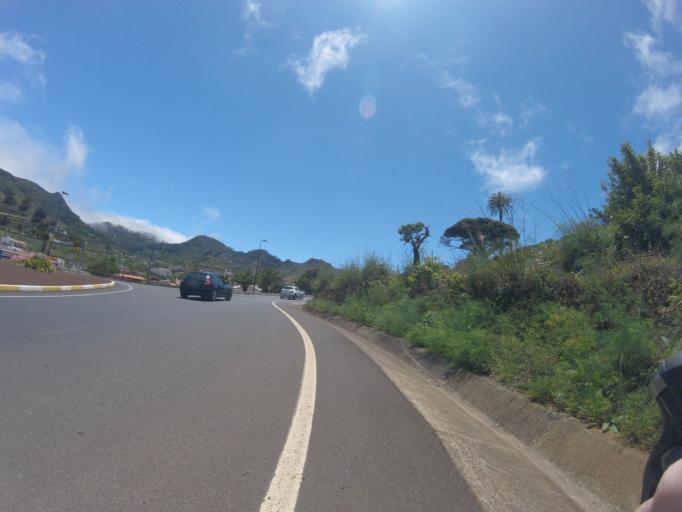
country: ES
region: Canary Islands
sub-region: Provincia de Santa Cruz de Tenerife
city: Tegueste
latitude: 28.5183
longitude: -16.3244
